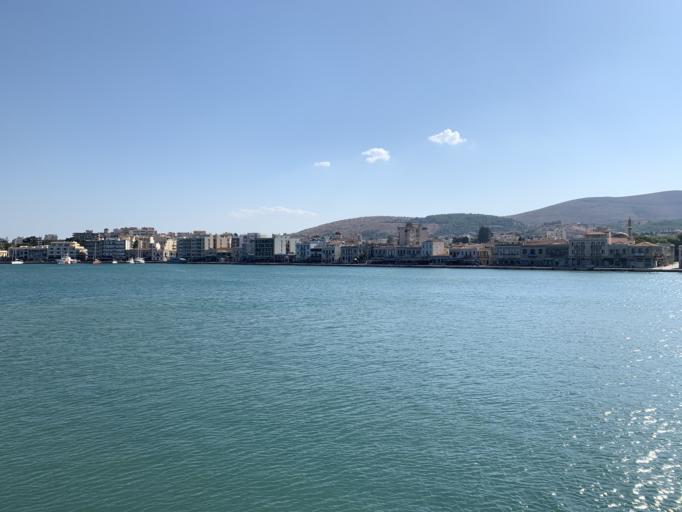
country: GR
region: North Aegean
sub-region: Chios
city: Chios
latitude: 38.3720
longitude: 26.1404
